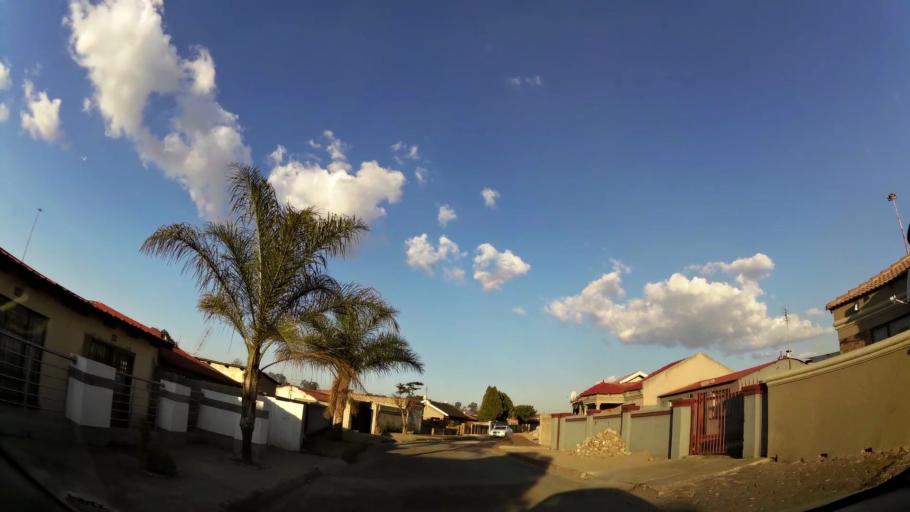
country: ZA
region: Mpumalanga
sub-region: Nkangala District Municipality
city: Witbank
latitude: -25.8766
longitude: 29.1930
